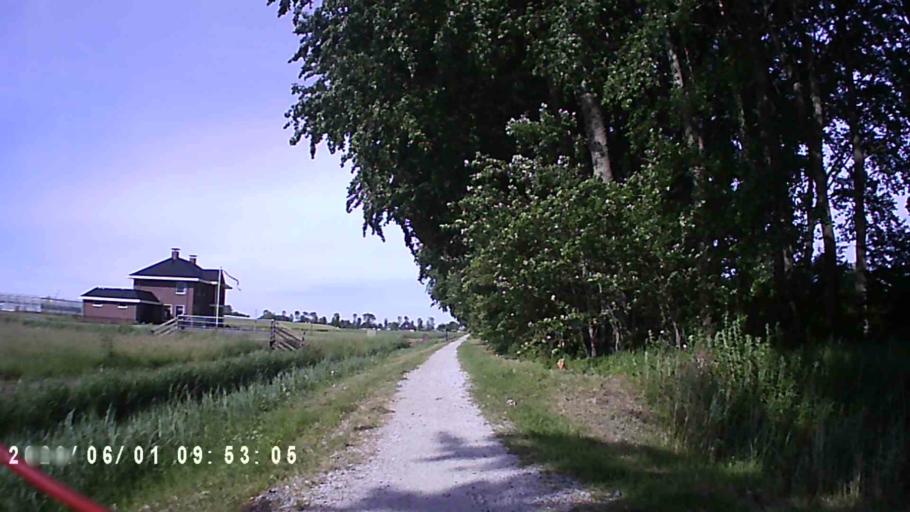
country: NL
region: Friesland
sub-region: Menameradiel
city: Berltsum
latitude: 53.2408
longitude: 5.6576
